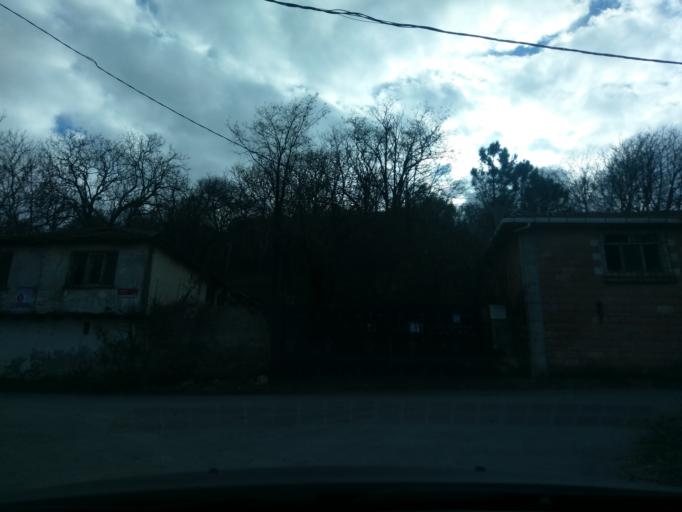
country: TR
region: Istanbul
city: Durusu
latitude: 41.2689
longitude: 28.6854
